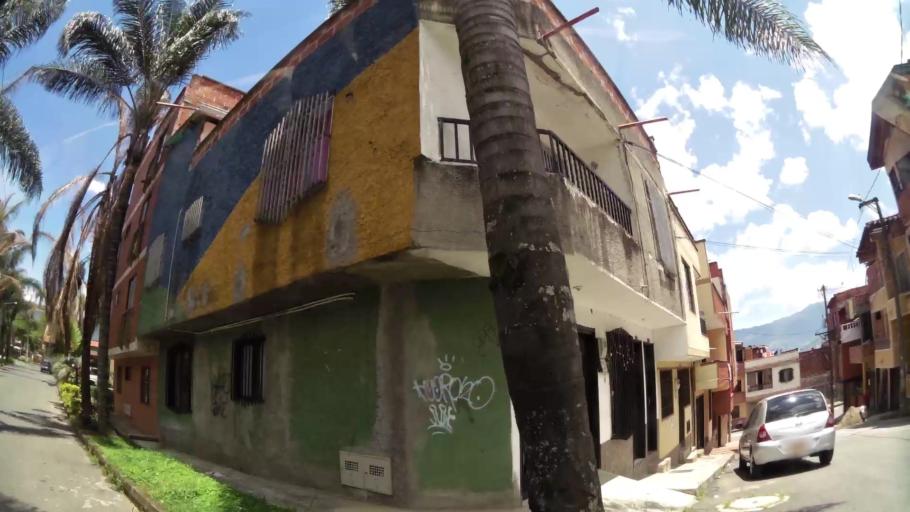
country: CO
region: Antioquia
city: La Estrella
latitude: 6.1608
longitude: -75.6401
